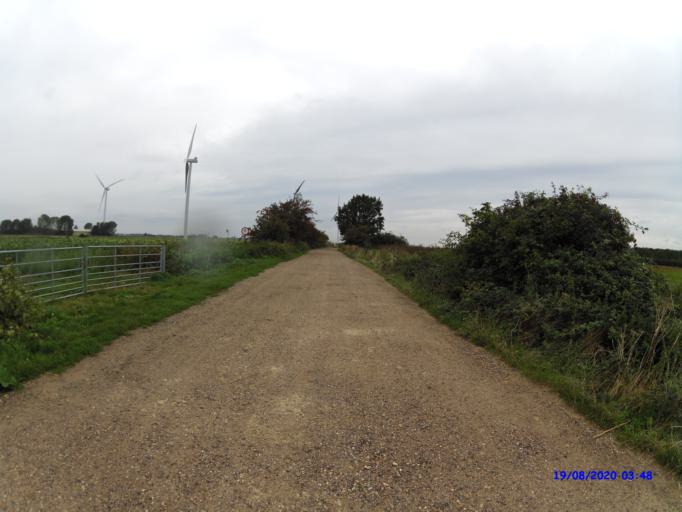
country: GB
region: England
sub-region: Cambridgeshire
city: Ramsey
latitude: 52.4612
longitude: -0.1120
